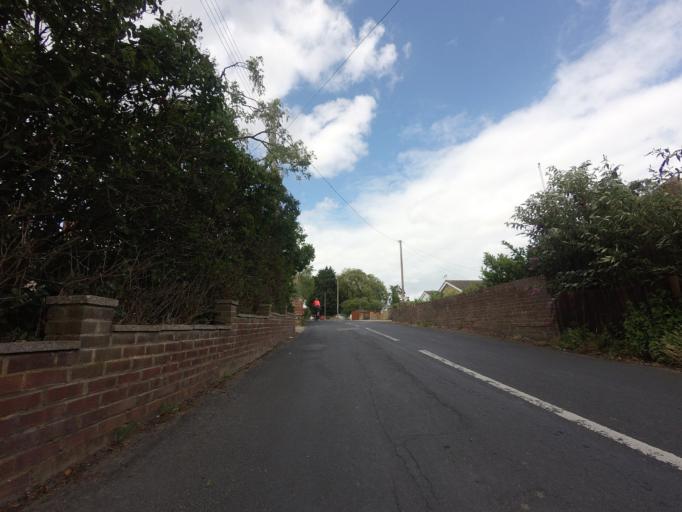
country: GB
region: England
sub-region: Medway
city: Stoke
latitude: 51.4540
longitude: 0.6345
